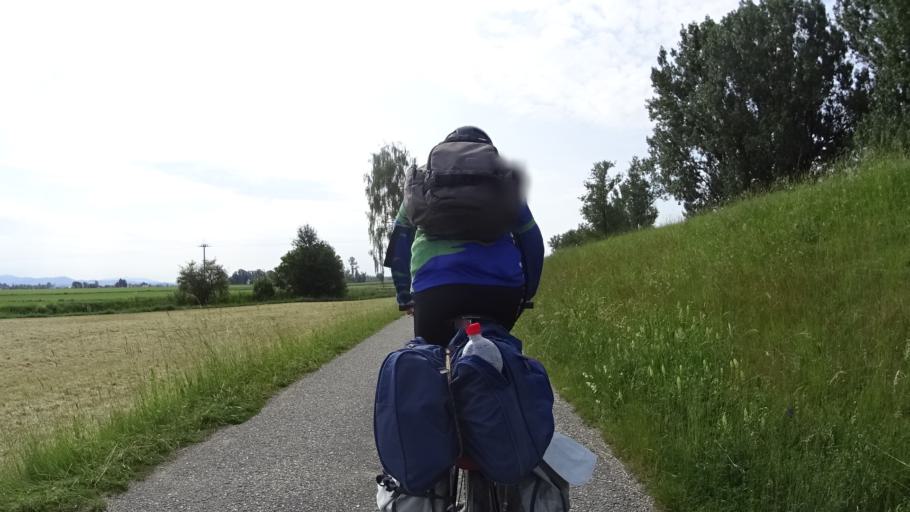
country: DE
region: Bavaria
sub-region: Lower Bavaria
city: Irlbach
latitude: 48.8380
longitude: 12.7755
